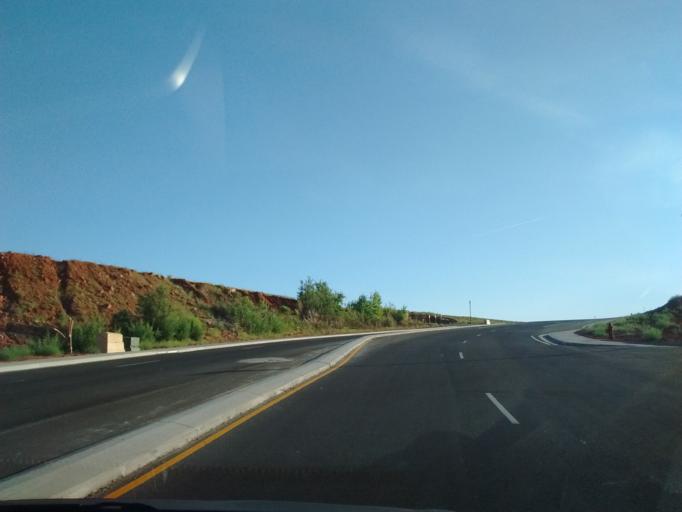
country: US
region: Utah
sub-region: Washington County
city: Washington
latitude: 37.1417
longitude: -113.4909
